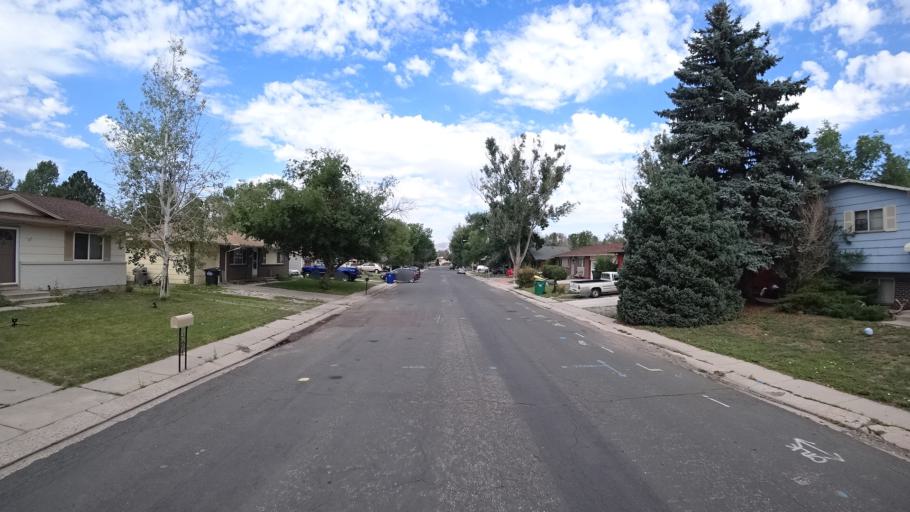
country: US
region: Colorado
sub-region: El Paso County
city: Cimarron Hills
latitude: 38.8989
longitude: -104.7563
